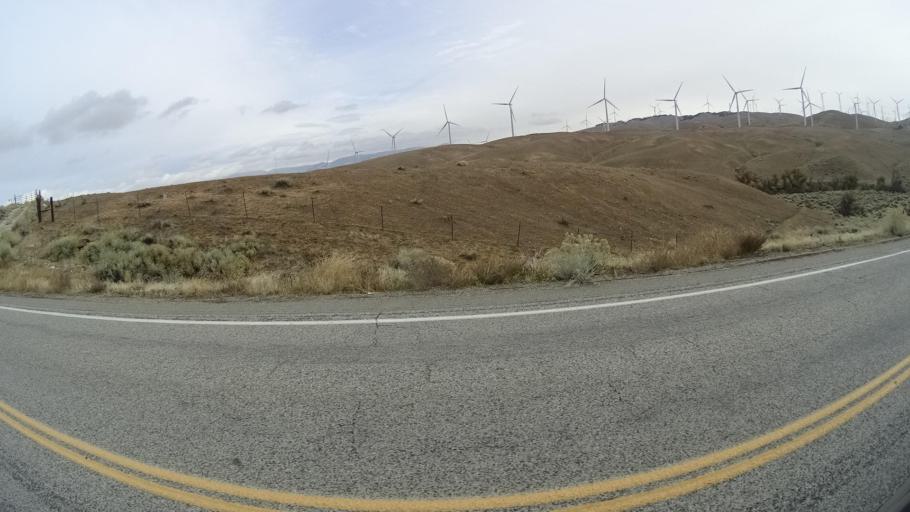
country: US
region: California
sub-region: Kern County
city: Tehachapi
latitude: 35.0875
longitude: -118.3958
